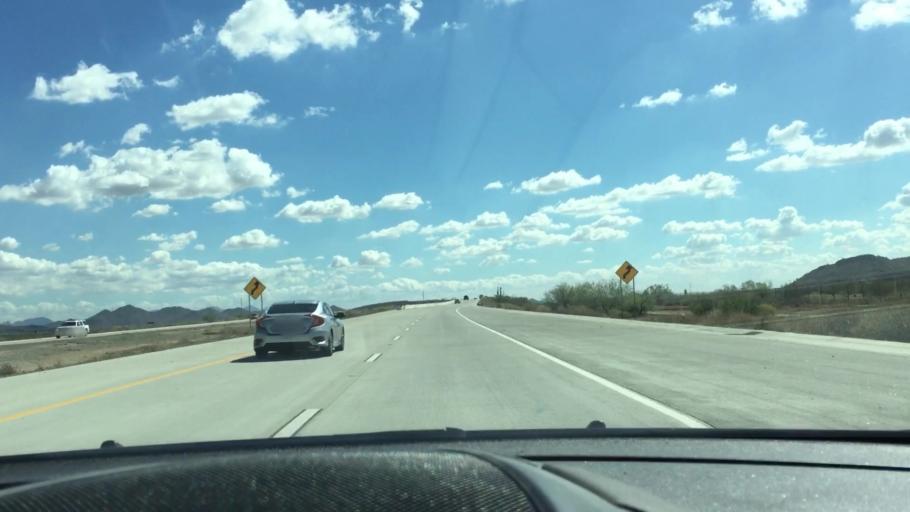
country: US
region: Arizona
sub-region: Maricopa County
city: Anthem
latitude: 33.7733
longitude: -112.1779
